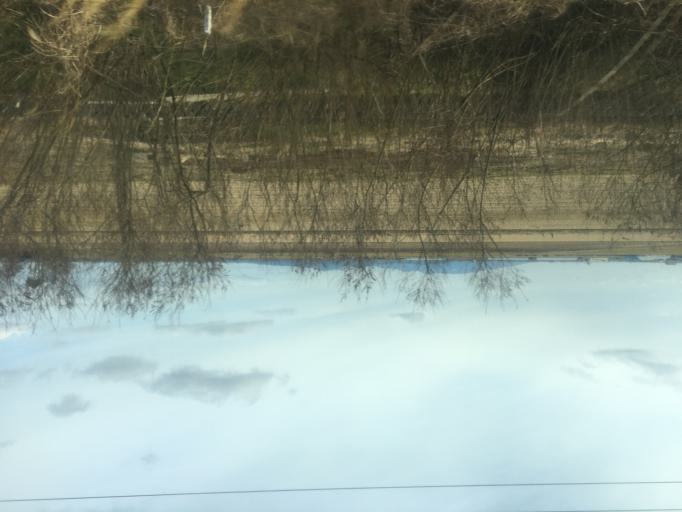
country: JP
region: Akita
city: Tenno
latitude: 39.9032
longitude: 140.0746
